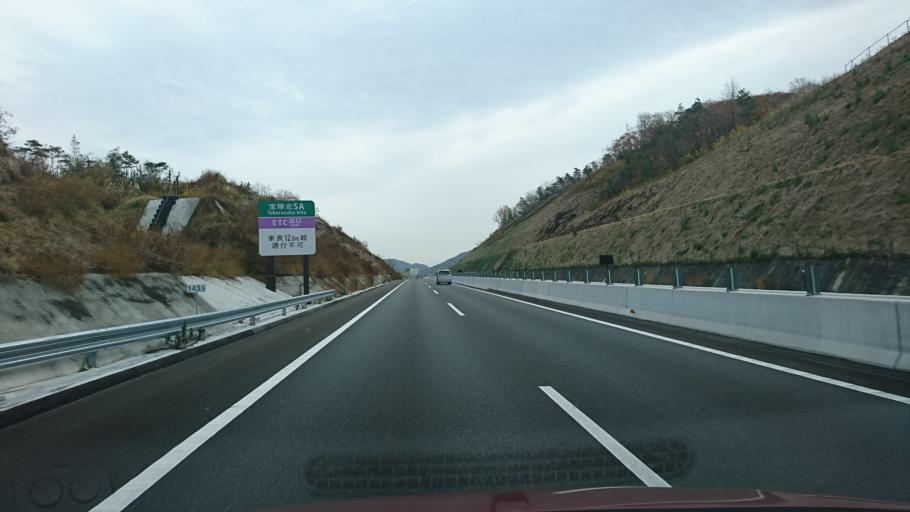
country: JP
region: Hyogo
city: Sandacho
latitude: 34.8642
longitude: 135.2848
